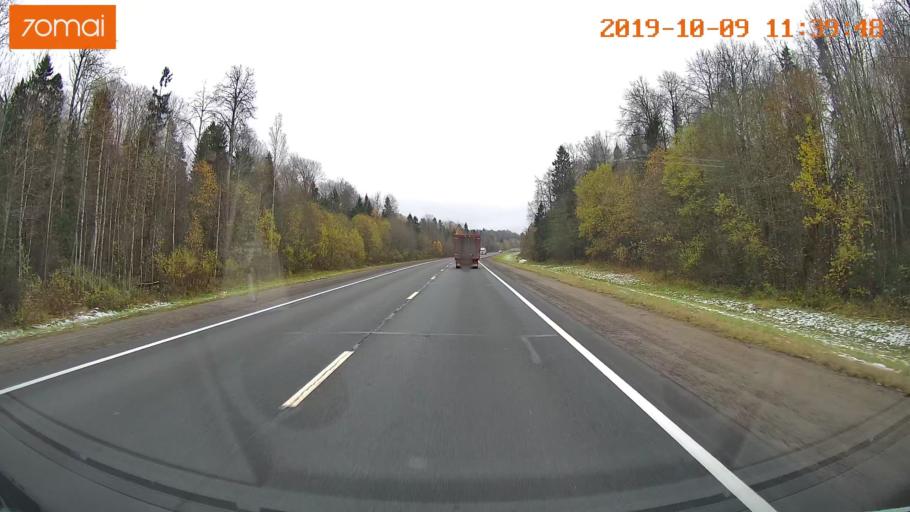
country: RU
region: Vologda
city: Gryazovets
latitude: 58.9518
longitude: 40.1695
